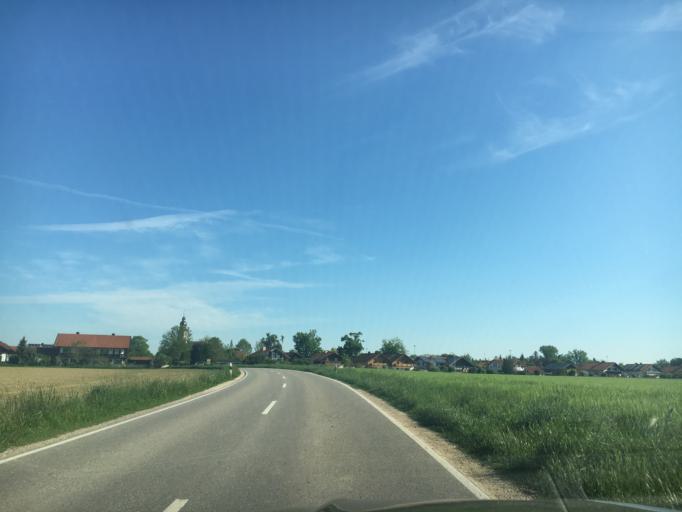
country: DE
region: Bavaria
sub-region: Upper Bavaria
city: Tacherting
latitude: 48.0765
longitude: 12.5979
